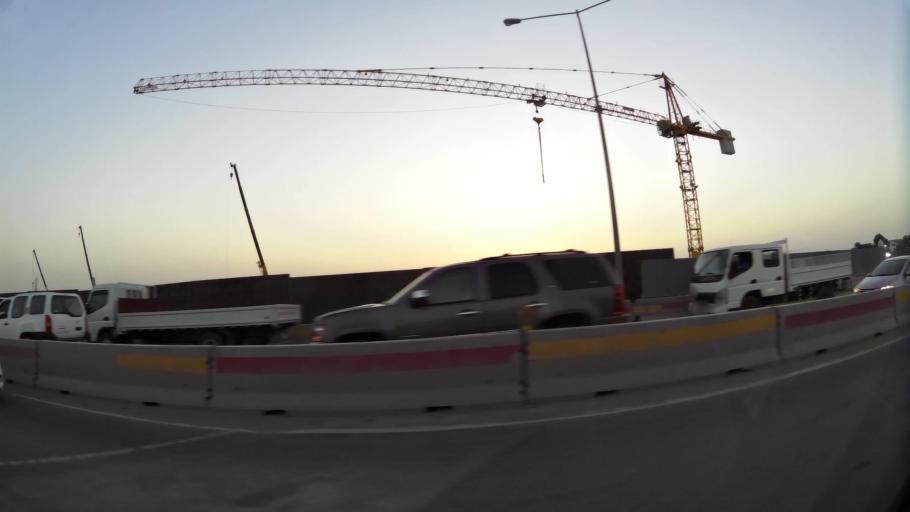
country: QA
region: Baladiyat ar Rayyan
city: Ar Rayyan
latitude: 25.2994
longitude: 51.4650
